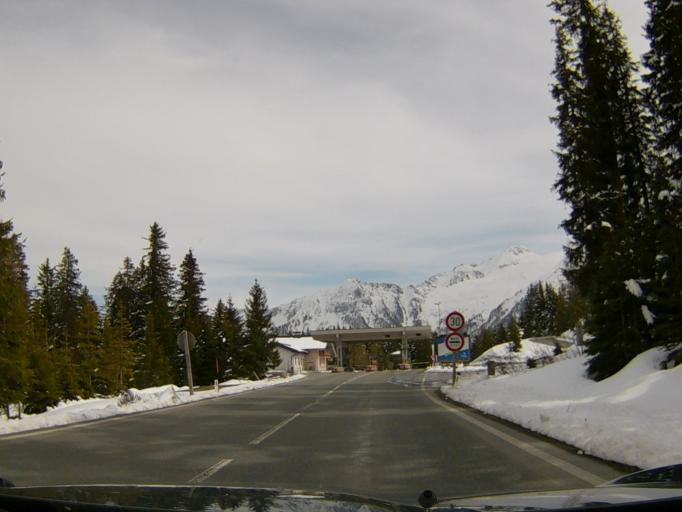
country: AT
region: Salzburg
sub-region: Politischer Bezirk Zell am See
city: Krimml
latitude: 47.2375
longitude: 12.1571
